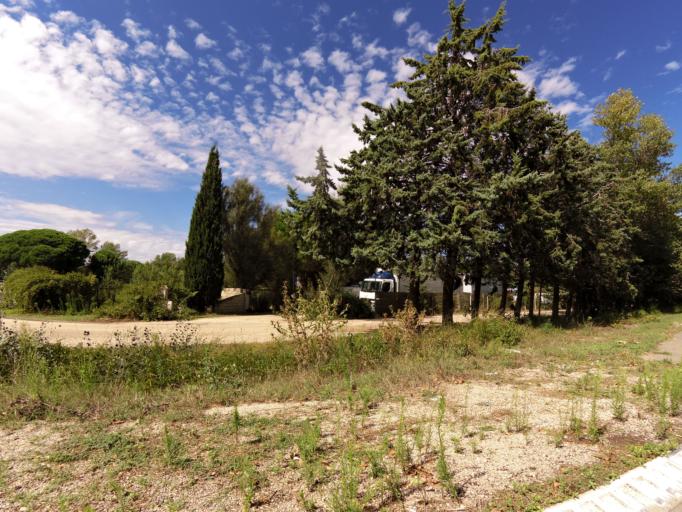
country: FR
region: Languedoc-Roussillon
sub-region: Departement du Gard
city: Aigues-Mortes
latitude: 43.5727
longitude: 4.1748
